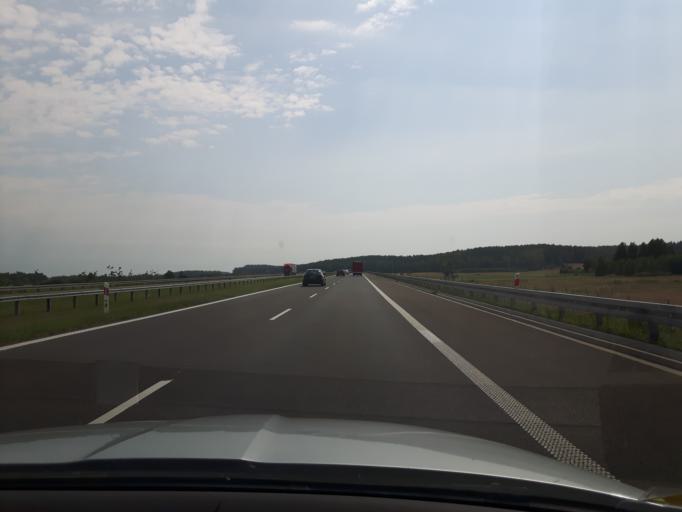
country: PL
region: Warmian-Masurian Voivodeship
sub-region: Powiat nidzicki
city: Nidzica
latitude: 53.3859
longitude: 20.3706
